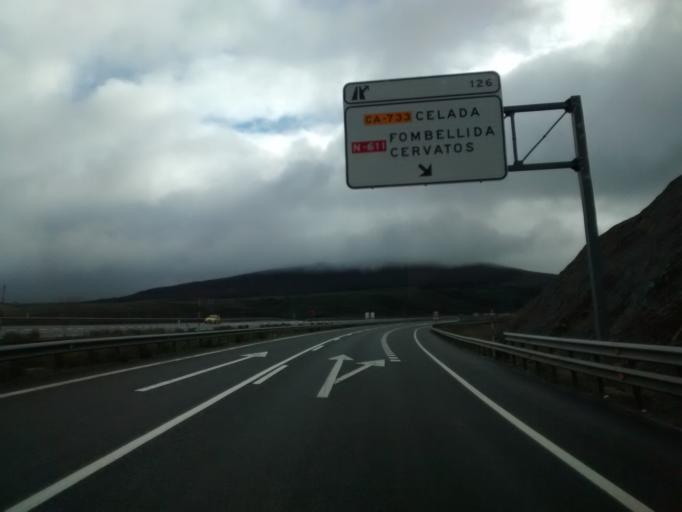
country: ES
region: Cantabria
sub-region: Provincia de Cantabria
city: Villaescusa
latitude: 42.9465
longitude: -4.1322
